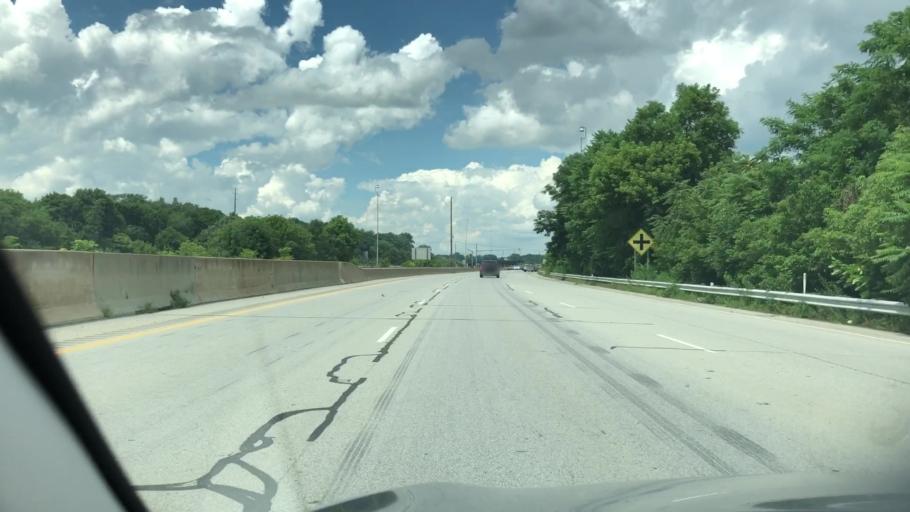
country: US
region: Ohio
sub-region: Stark County
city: Massillon
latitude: 40.7857
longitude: -81.5204
